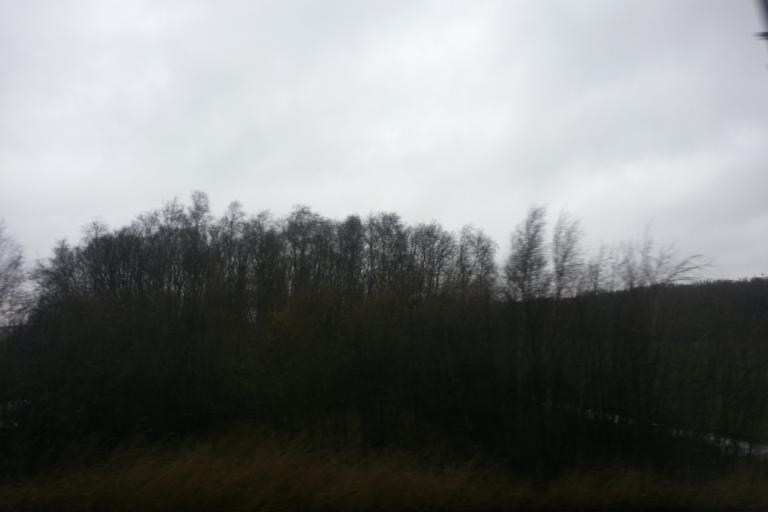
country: NL
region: South Holland
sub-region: Gemeente Wassenaar
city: Wassenaar
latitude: 52.1025
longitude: 4.3959
